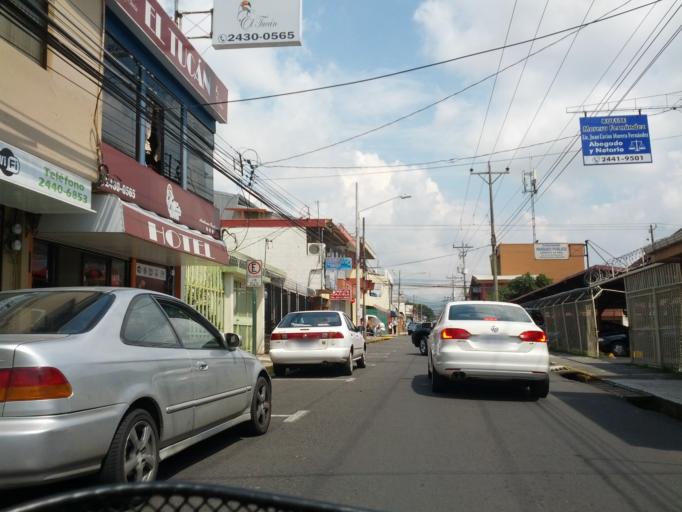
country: CR
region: Alajuela
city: Alajuela
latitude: 10.0185
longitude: -84.2146
